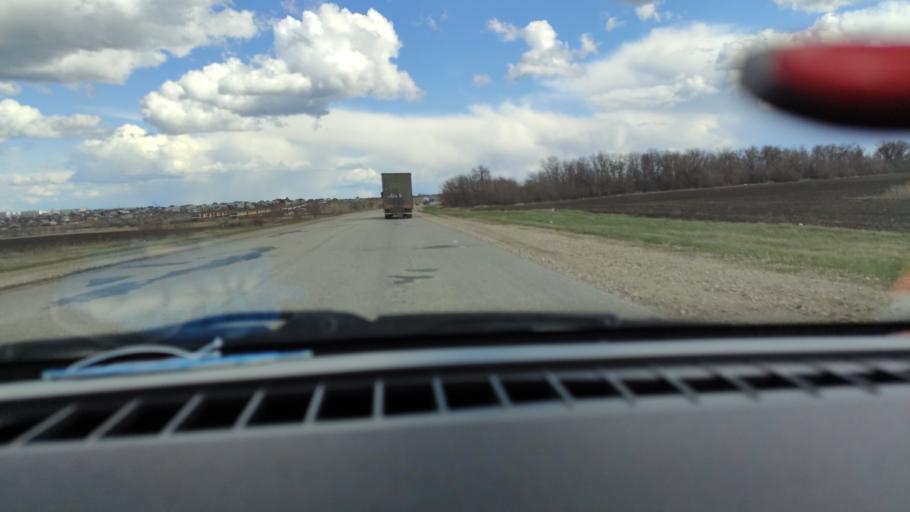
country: RU
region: Samara
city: Varlamovo
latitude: 53.1164
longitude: 48.3450
